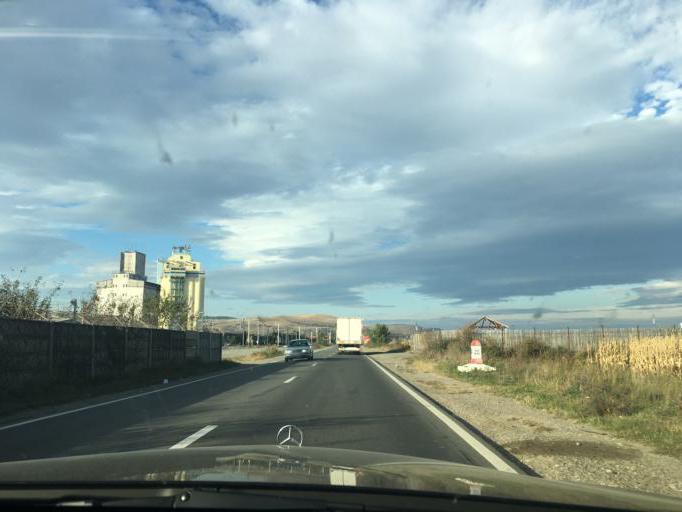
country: RO
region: Alba
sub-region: Municipiul Alba Iulia
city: Barabant
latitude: 46.0848
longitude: 23.5974
